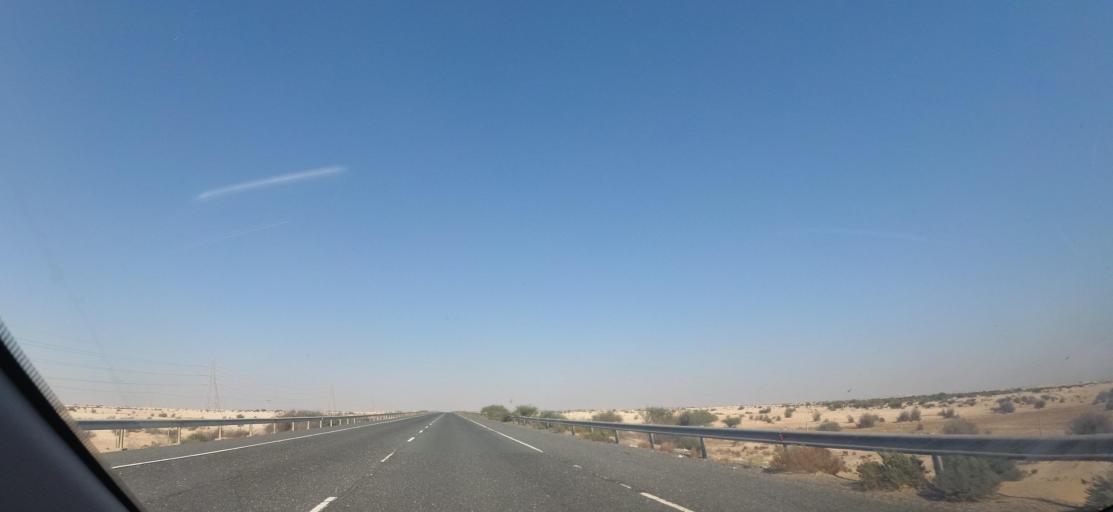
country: QA
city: Al Jumayliyah
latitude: 25.5850
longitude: 51.0597
